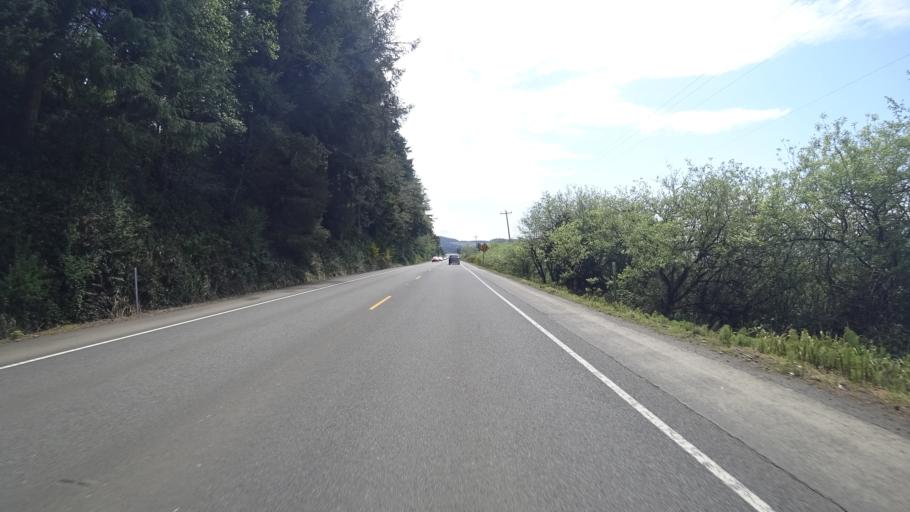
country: US
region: Oregon
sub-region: Lincoln County
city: Lincoln City
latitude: 44.9095
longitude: -124.0057
